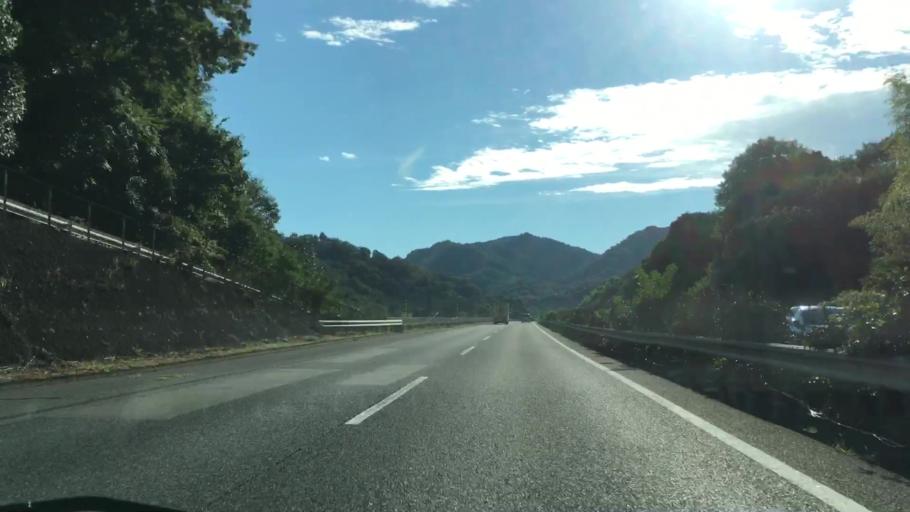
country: JP
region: Yamaguchi
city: Yanai
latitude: 34.0646
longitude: 132.0502
